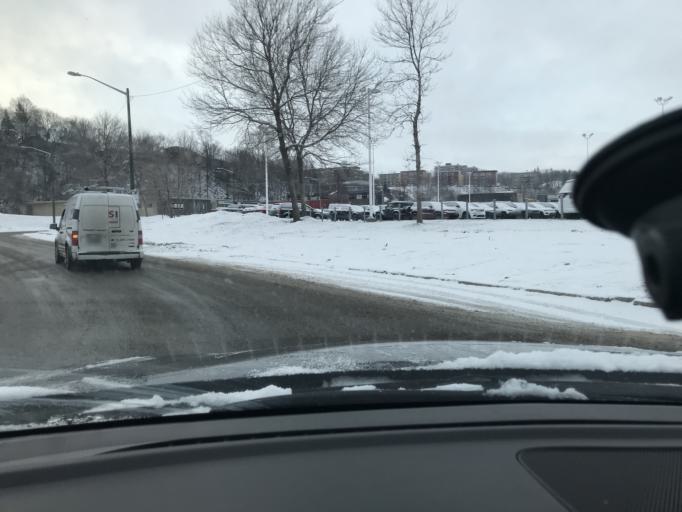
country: CA
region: Quebec
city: Quebec
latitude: 46.7954
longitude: -71.2707
